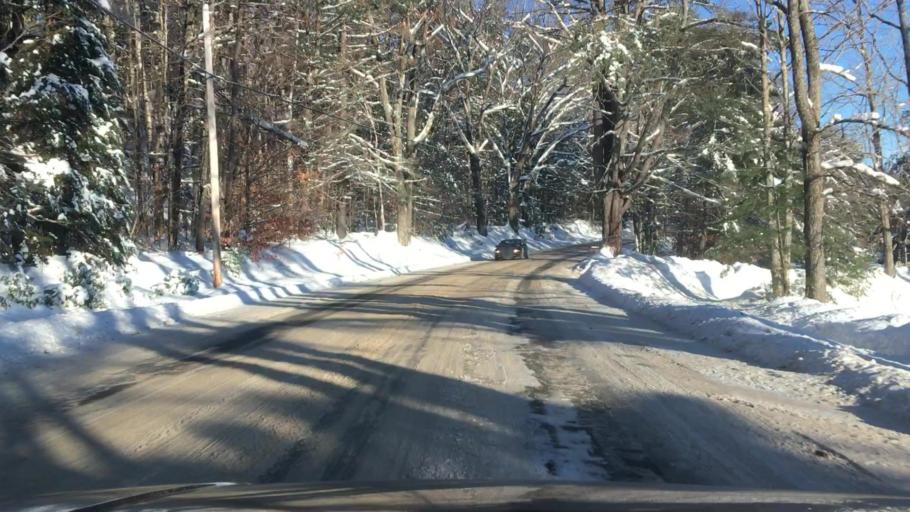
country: US
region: Maine
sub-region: Oxford County
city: Lovell
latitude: 44.1426
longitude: -70.9796
